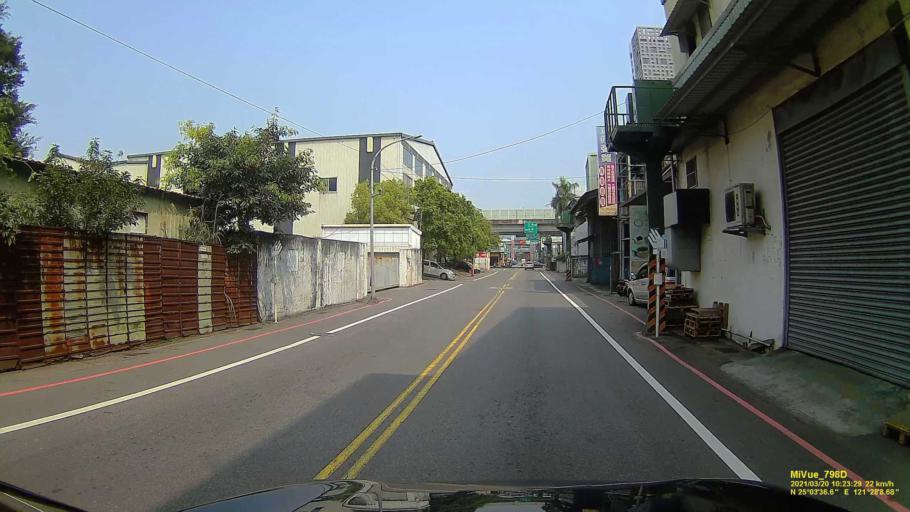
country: TW
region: Taipei
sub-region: Taipei
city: Banqiao
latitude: 25.0603
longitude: 121.4690
